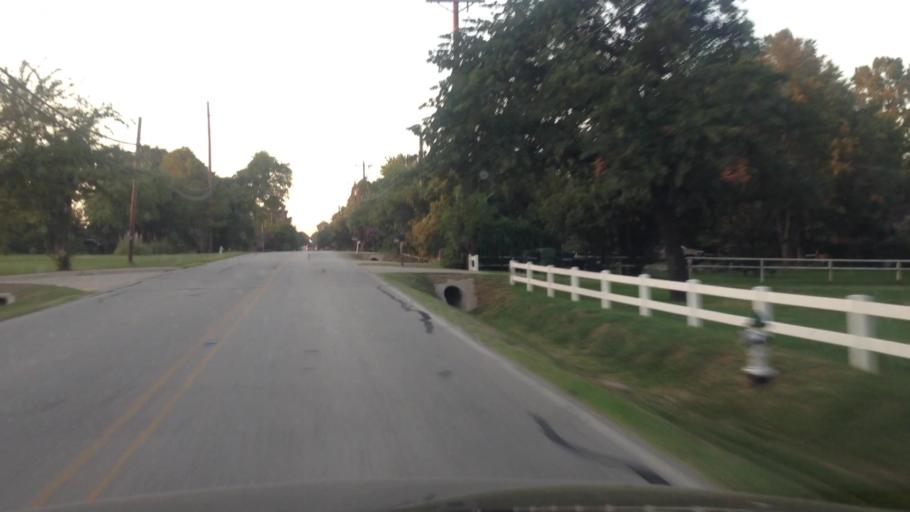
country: US
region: Texas
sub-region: Tarrant County
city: Keller
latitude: 32.9388
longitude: -97.2032
